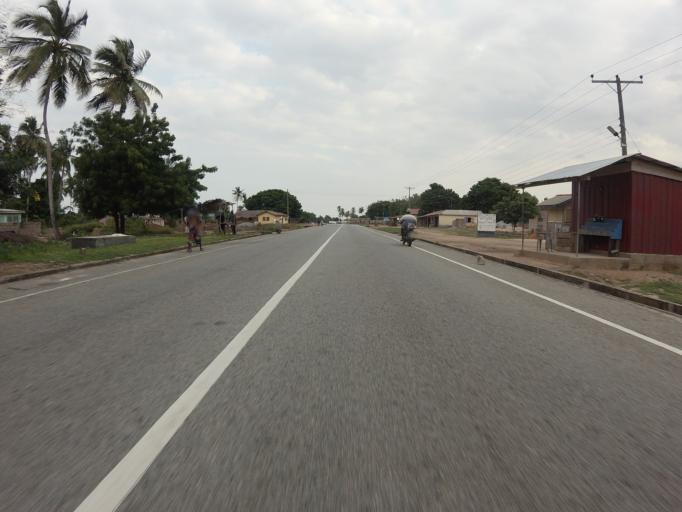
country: GH
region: Volta
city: Ho
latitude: 6.2358
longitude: 0.5511
